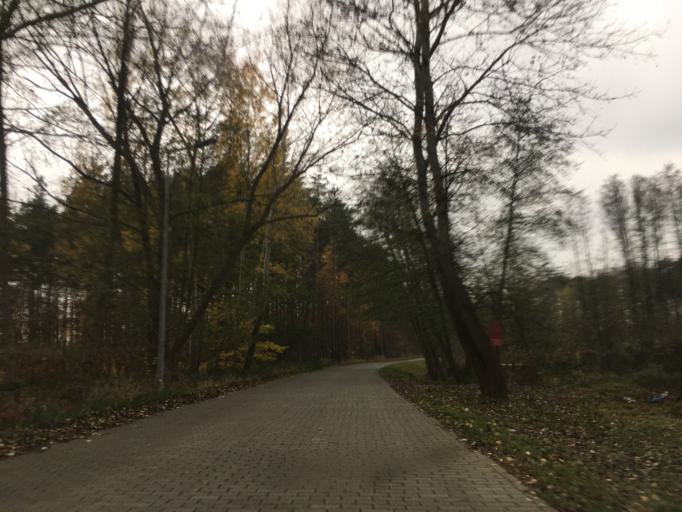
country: PL
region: Masovian Voivodeship
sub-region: Powiat piaseczynski
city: Lesznowola
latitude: 52.0424
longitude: 20.9389
